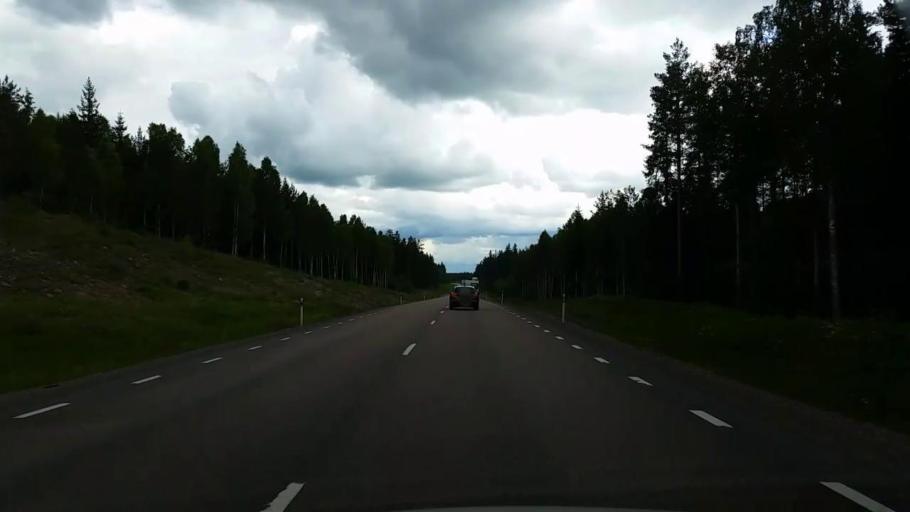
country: SE
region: Dalarna
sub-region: Avesta Kommun
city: Horndal
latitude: 60.4555
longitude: 16.4450
